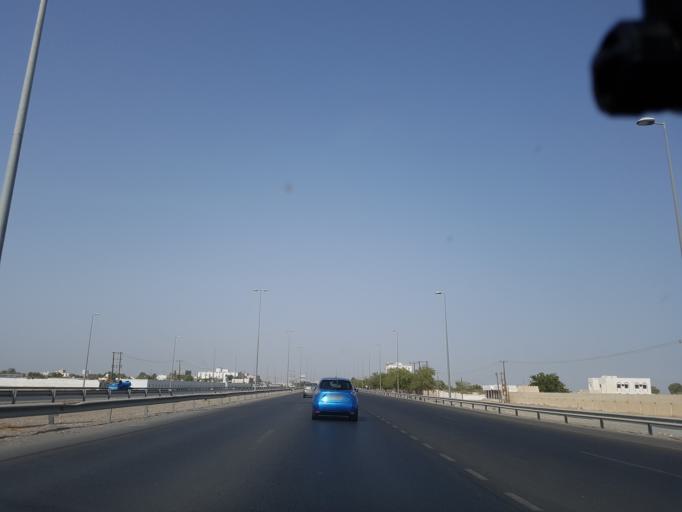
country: OM
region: Al Batinah
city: Barka'
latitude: 23.6841
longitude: 58.0181
